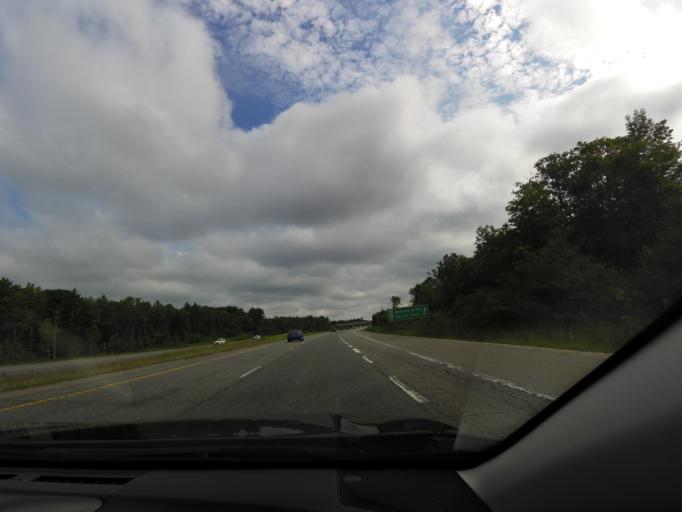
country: CA
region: Ontario
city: Gravenhurst
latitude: 44.9338
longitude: -79.3438
